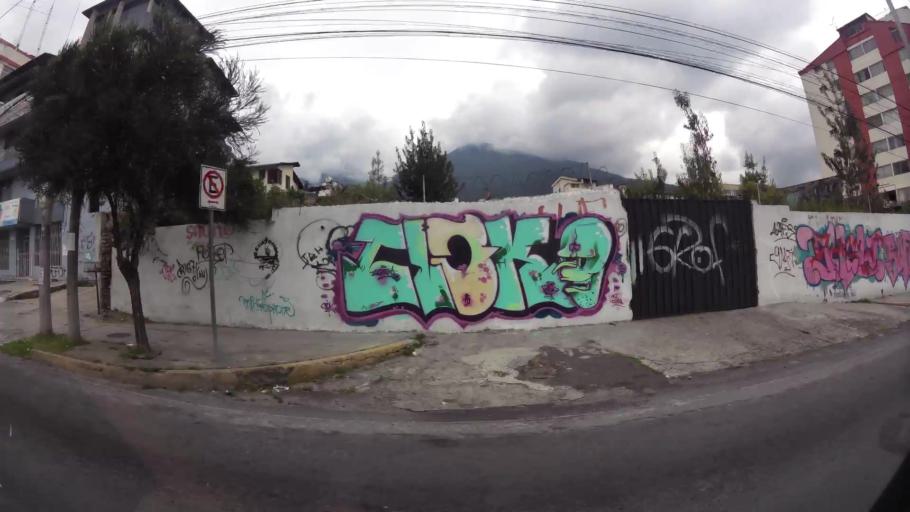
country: EC
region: Pichincha
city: Quito
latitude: -0.1759
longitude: -78.4938
